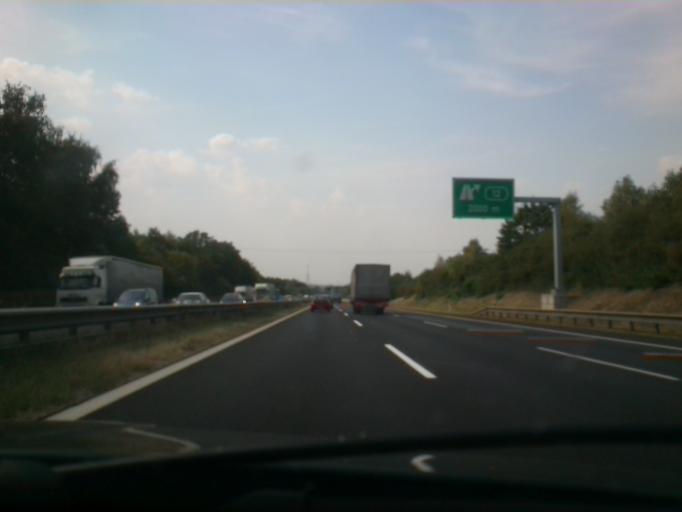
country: CZ
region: Central Bohemia
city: Velke Popovice
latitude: 49.9526
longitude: 14.6406
